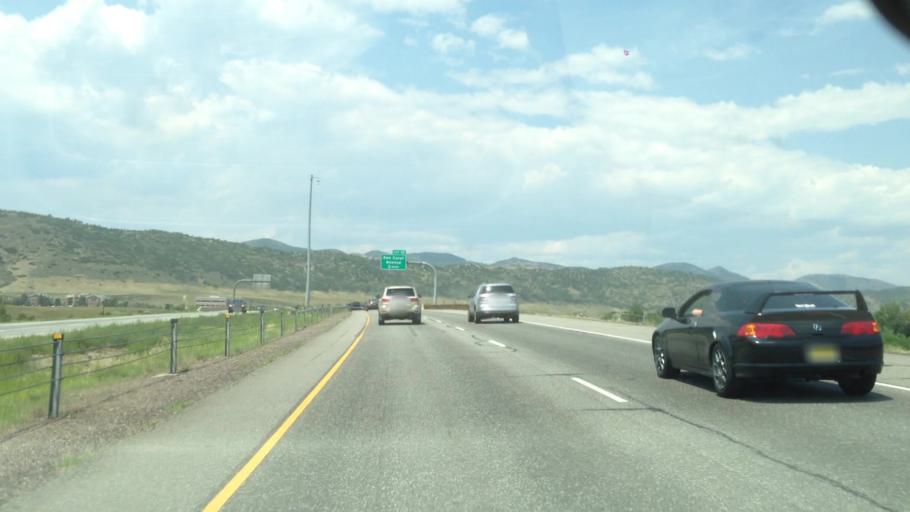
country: US
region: Colorado
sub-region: Jefferson County
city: Ken Caryl
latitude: 39.5604
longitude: -105.1075
